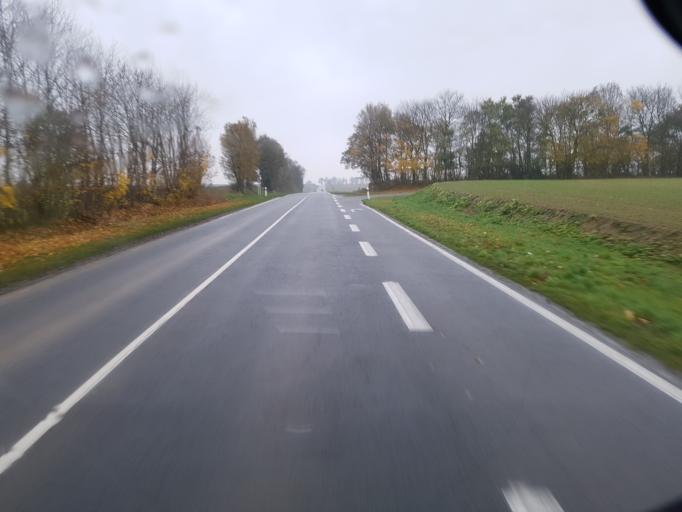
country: FR
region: Picardie
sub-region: Departement de l'Aisne
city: Omissy
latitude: 49.8979
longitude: 3.2627
